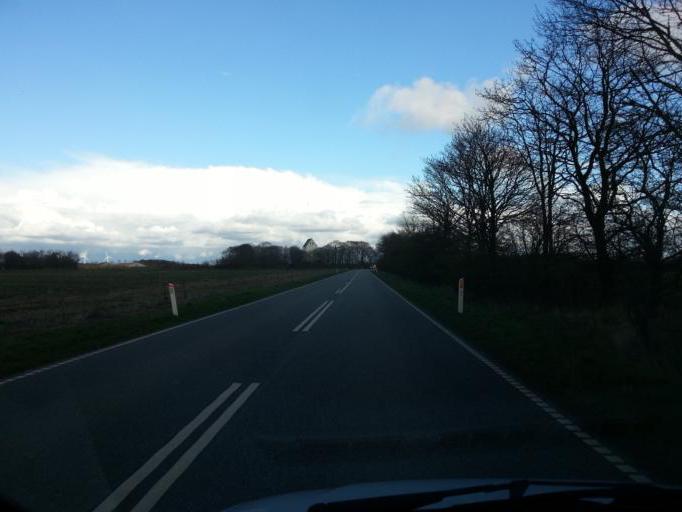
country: DK
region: Central Jutland
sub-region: Ringkobing-Skjern Kommune
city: Tarm
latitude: 55.8862
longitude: 8.5199
